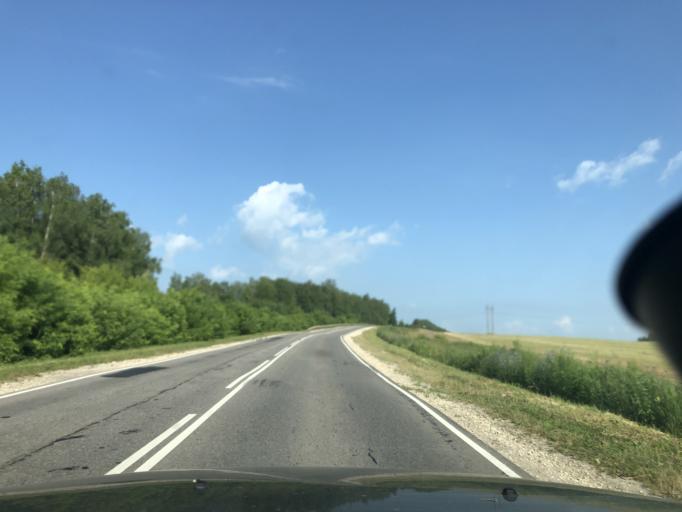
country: RU
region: Tula
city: Dubna
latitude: 54.1156
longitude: 37.0849
